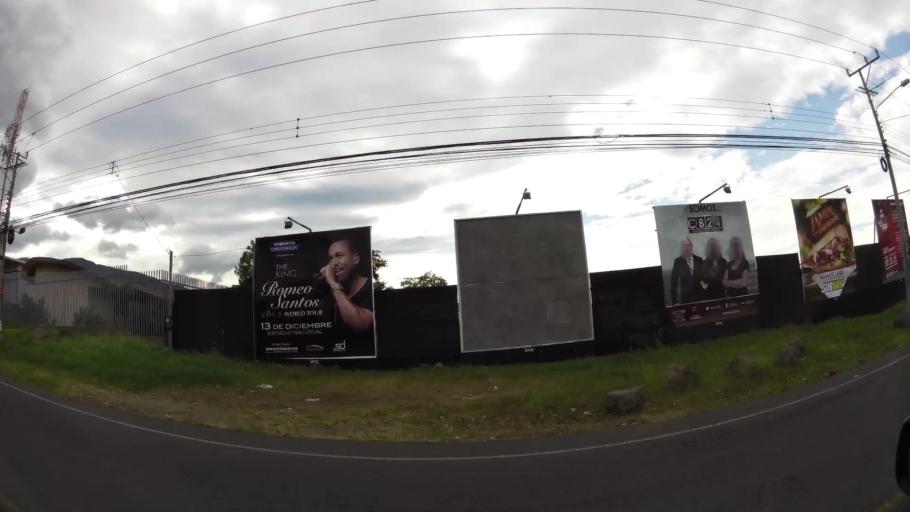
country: CR
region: San Jose
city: Santa Ana
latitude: 9.9409
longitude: -84.1894
